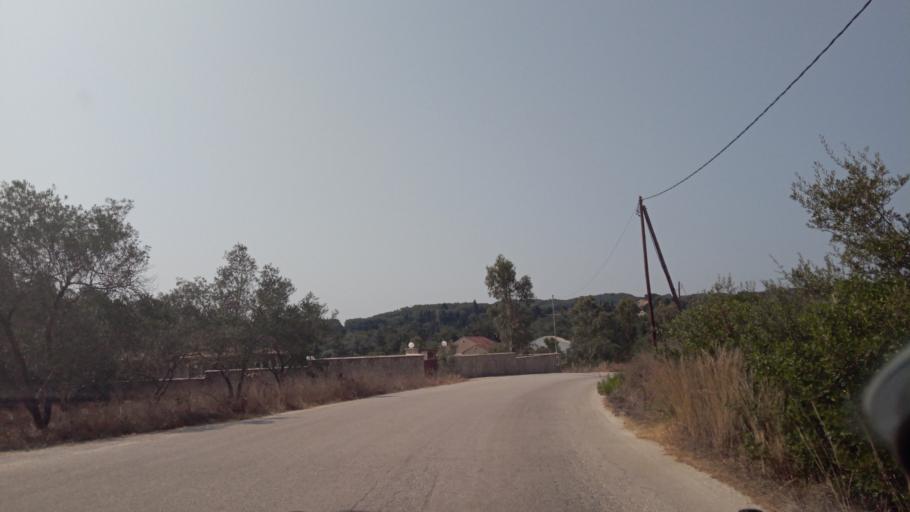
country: GR
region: Ionian Islands
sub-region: Nomos Kerkyras
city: Perivoli
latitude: 39.4143
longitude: 20.0295
